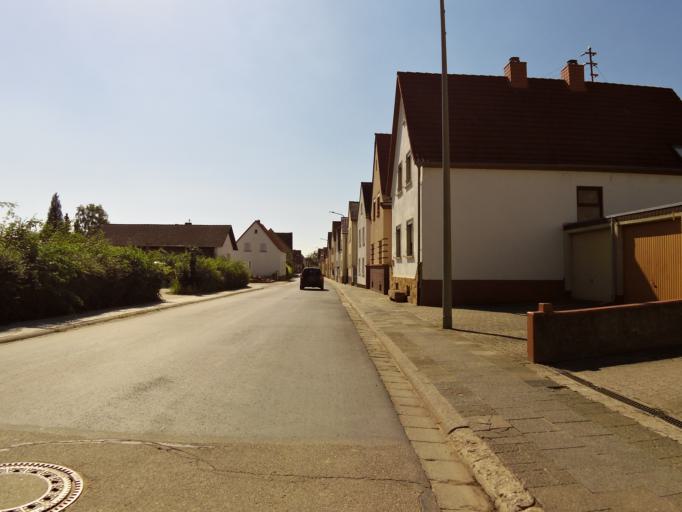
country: DE
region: Rheinland-Pfalz
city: Bohl-Iggelheim
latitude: 49.3868
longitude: 8.2902
